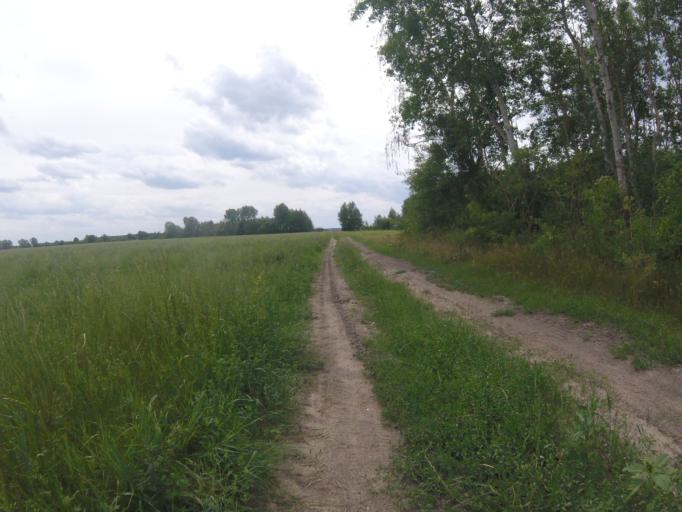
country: DE
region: Brandenburg
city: Bestensee
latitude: 52.2650
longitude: 13.7144
